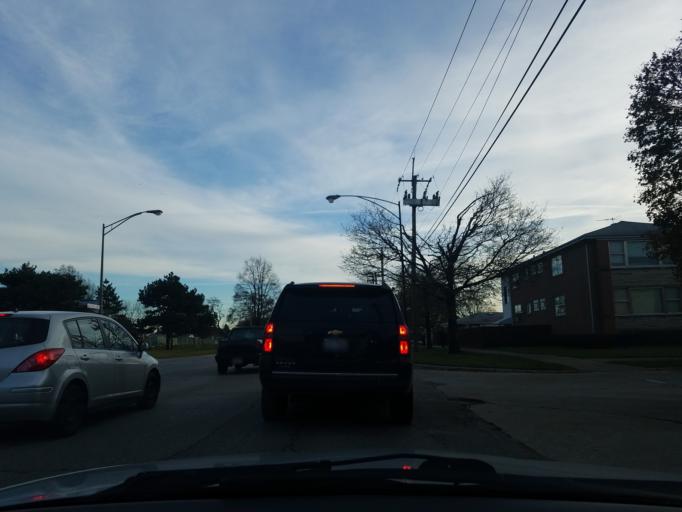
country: US
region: Illinois
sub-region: Cook County
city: Norridge
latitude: 41.9753
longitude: -87.8367
